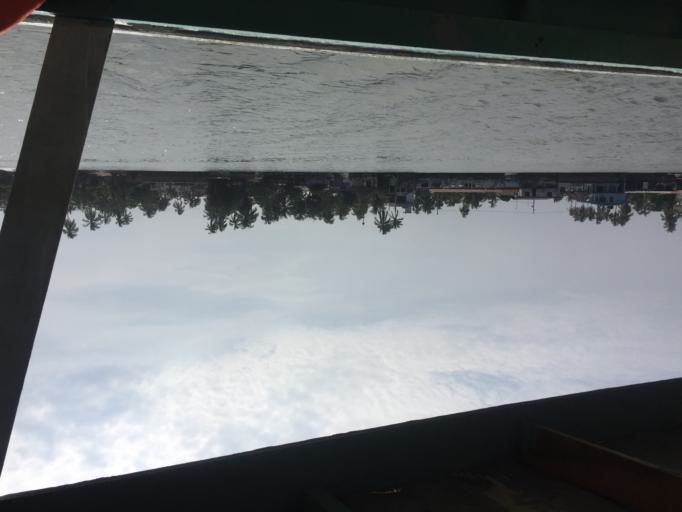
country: MX
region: Guerrero
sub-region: Coyuca de Benitez
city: Colonia Luces en el Mar
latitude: 16.9025
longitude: -99.9692
